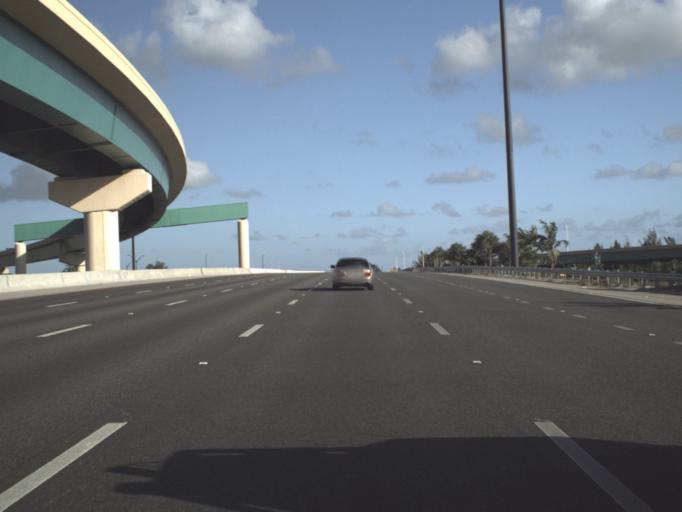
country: US
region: Florida
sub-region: Broward County
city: Broadview Park
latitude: 26.0884
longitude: -80.2162
